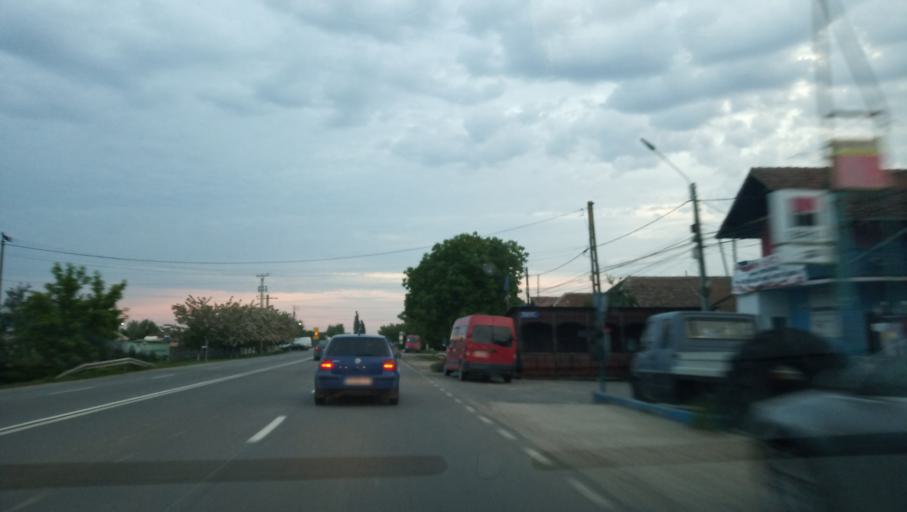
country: RO
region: Timis
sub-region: Comuna Sag
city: Sag
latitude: 45.6528
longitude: 21.1743
